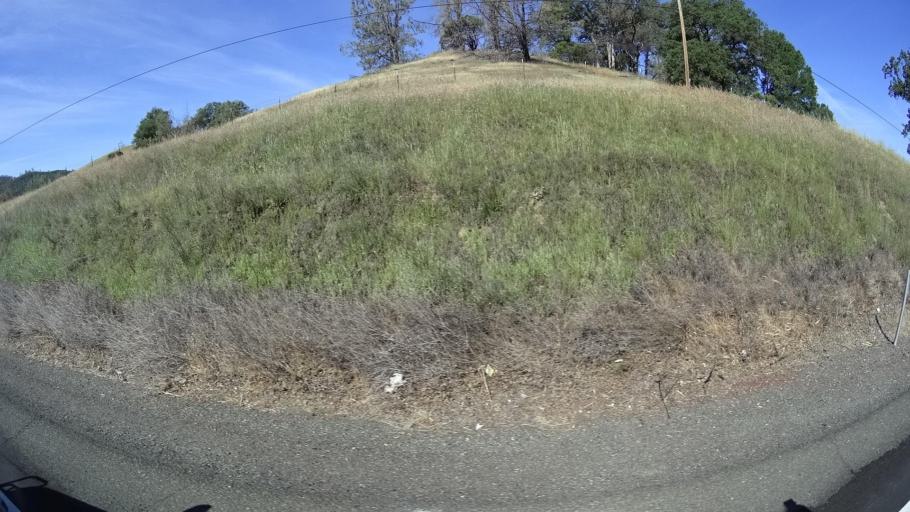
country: US
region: California
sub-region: Lake County
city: Kelseyville
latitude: 38.9509
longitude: -122.8262
